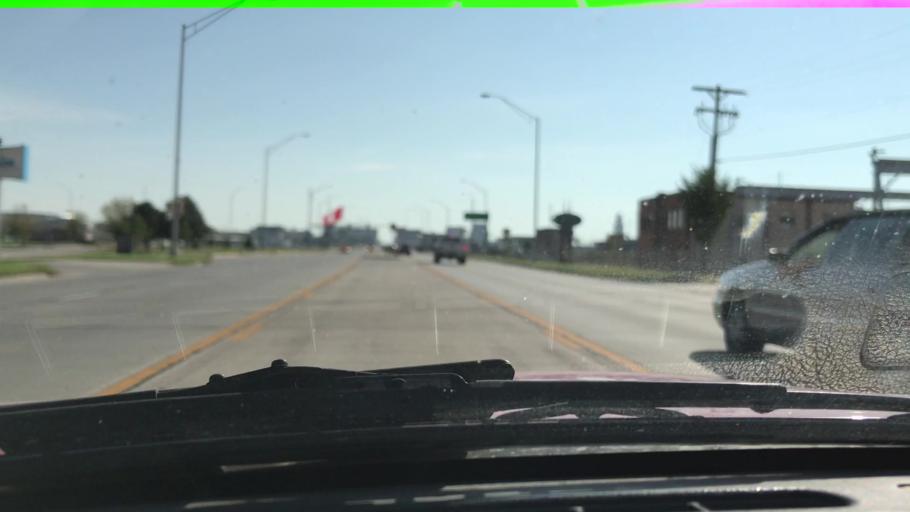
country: US
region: Nebraska
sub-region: Lancaster County
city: Lincoln
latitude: 40.8137
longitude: -96.7276
